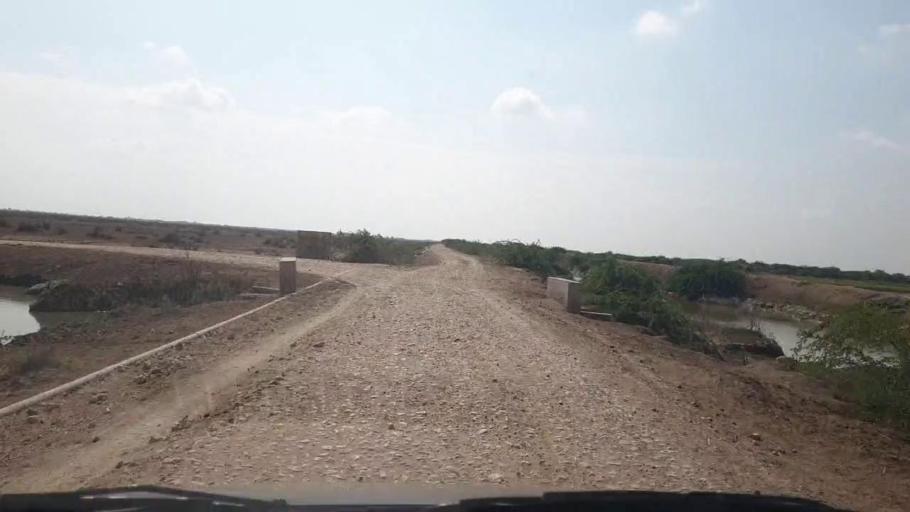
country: PK
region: Sindh
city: Badin
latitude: 24.5070
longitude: 68.6081
